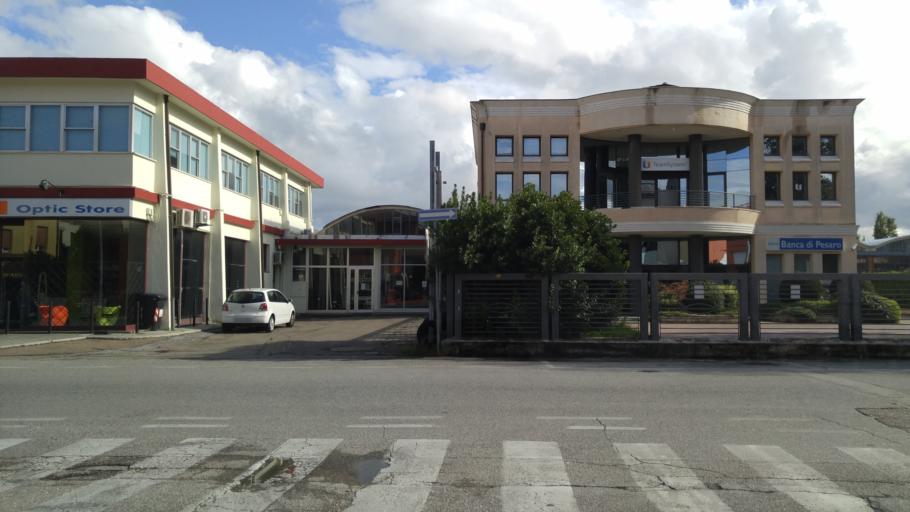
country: IT
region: The Marches
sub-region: Provincia di Pesaro e Urbino
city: Pesaro
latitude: 43.9068
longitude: 12.8924
